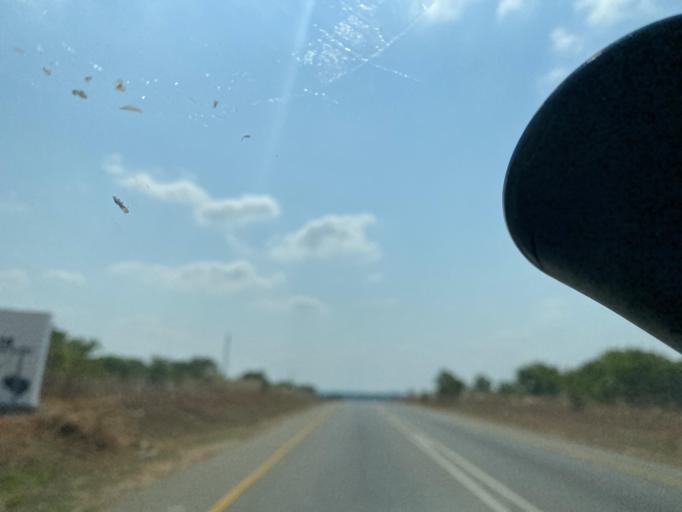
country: ZM
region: Lusaka
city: Chongwe
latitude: -15.5301
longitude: 28.6263
